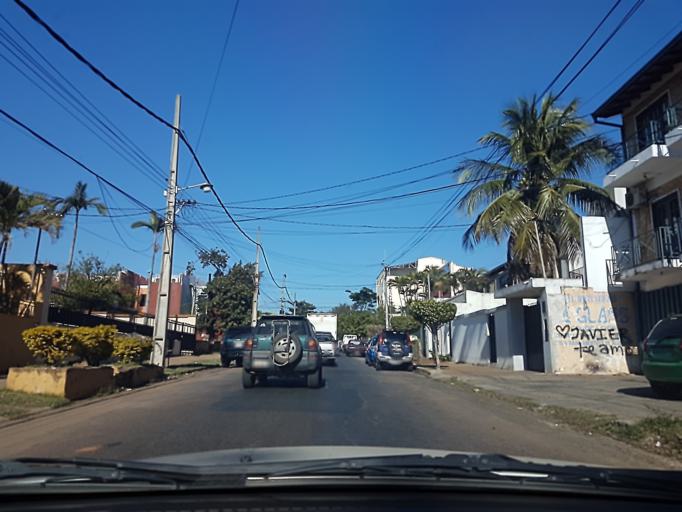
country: PY
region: Central
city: Lambare
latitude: -25.3135
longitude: -57.5862
